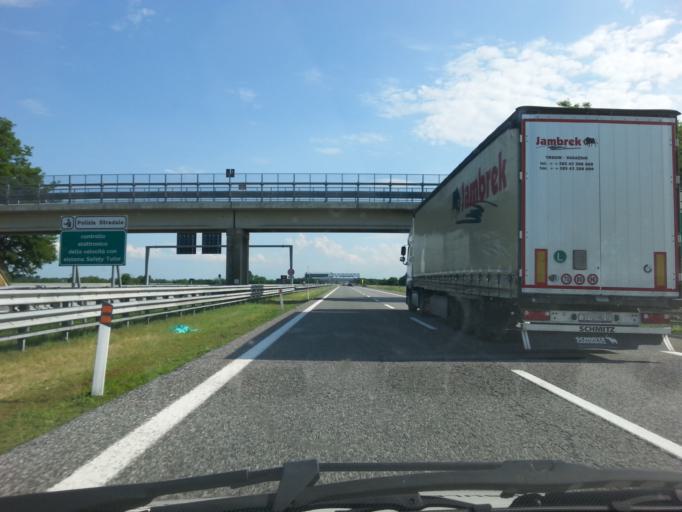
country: IT
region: Piedmont
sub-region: Provincia di Torino
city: Carmagnola
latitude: 44.8444
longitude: 7.7492
